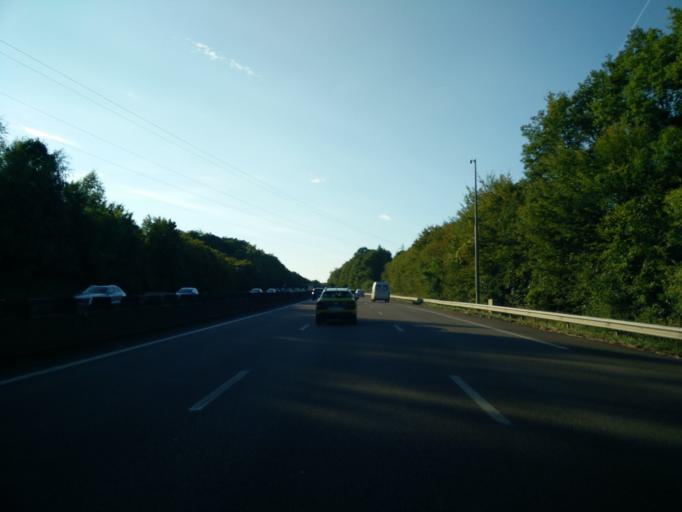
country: FR
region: Ile-de-France
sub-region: Departement des Yvelines
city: Rosny-sur-Seine
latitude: 48.9992
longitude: 1.6126
